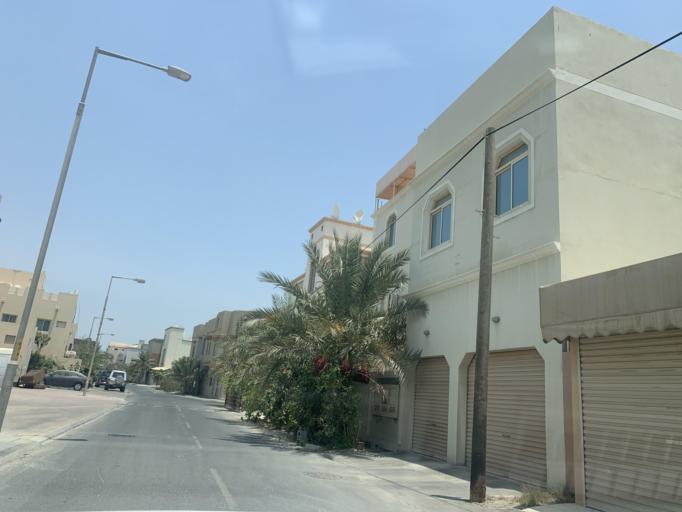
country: BH
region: Manama
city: Jidd Hafs
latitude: 26.2085
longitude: 50.4724
